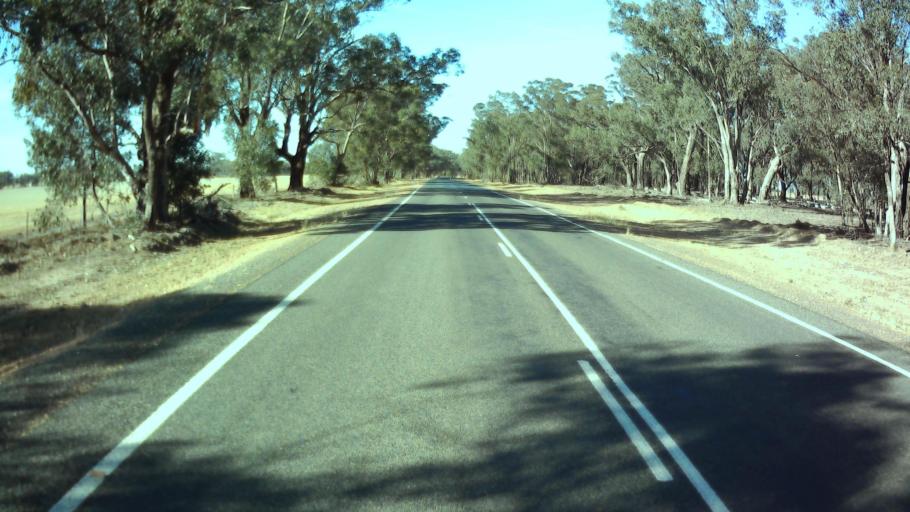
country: AU
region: New South Wales
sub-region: Weddin
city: Grenfell
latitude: -34.0050
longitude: 148.1242
